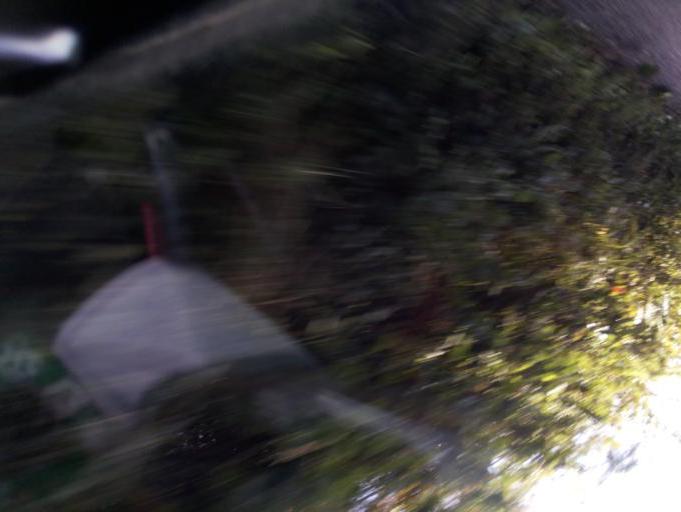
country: GB
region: England
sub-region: Devon
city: Totnes
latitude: 50.3460
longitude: -3.6982
